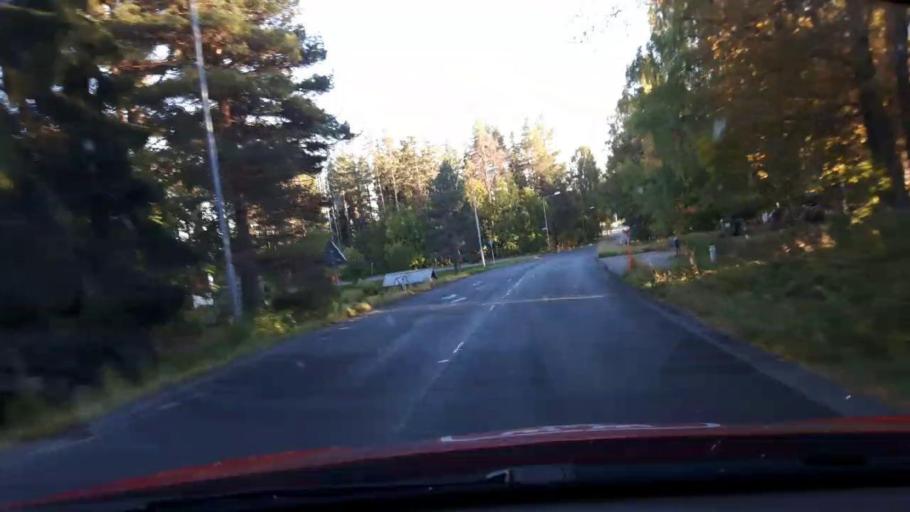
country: SE
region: Jaemtland
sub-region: OEstersunds Kommun
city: Lit
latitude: 63.3925
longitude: 14.9068
